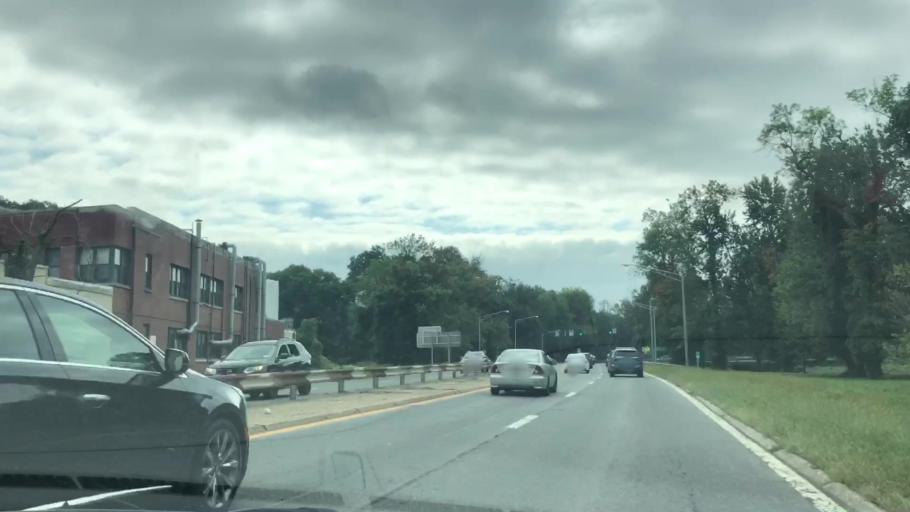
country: US
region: New York
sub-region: Westchester County
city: Hastings-on-Hudson
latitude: 40.9756
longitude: -73.8686
